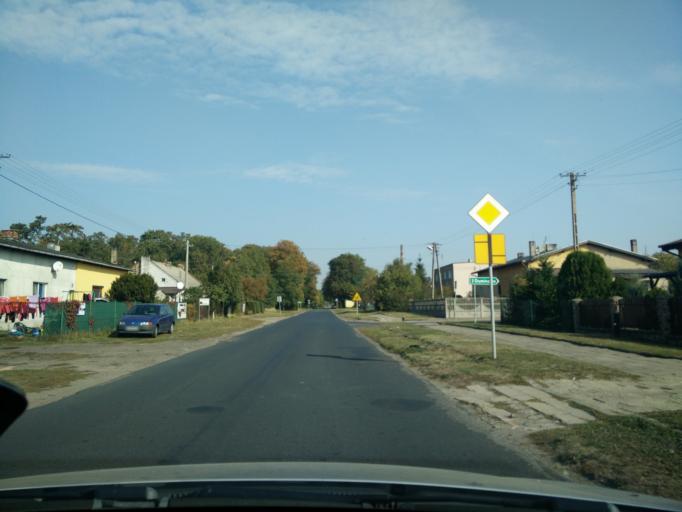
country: PL
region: Greater Poland Voivodeship
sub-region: Powiat sredzki
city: Dominowo
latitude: 52.3033
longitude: 17.3490
